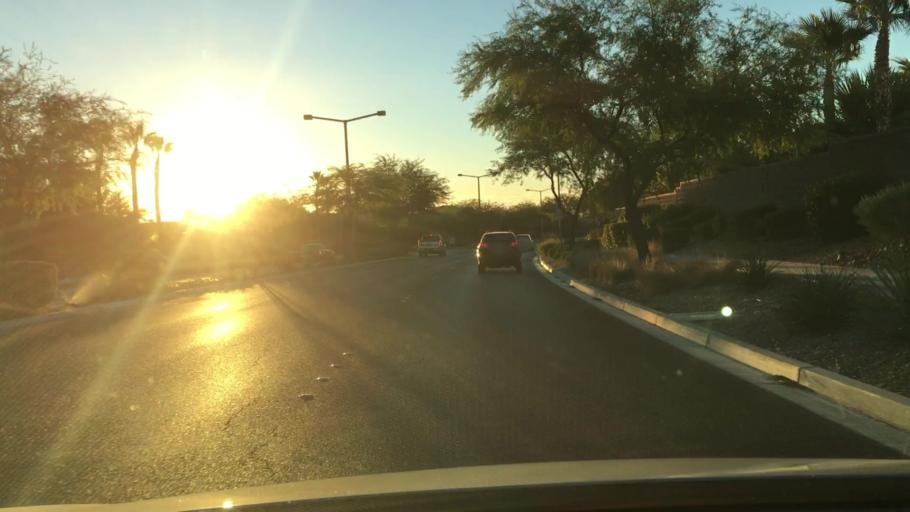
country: US
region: Nevada
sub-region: Clark County
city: Summerlin South
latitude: 36.1554
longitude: -115.3476
